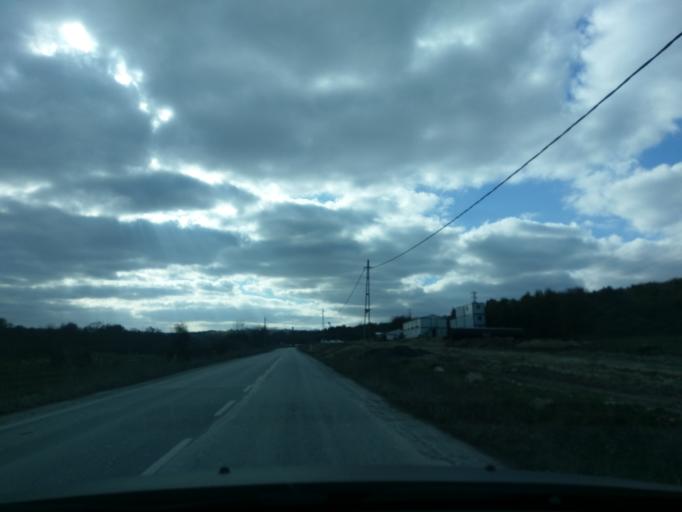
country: TR
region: Istanbul
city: Durusu
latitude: 41.2952
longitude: 28.6679
